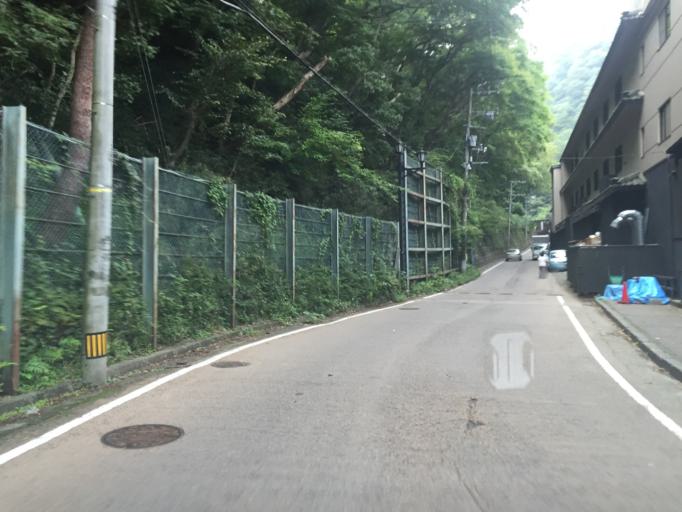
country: JP
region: Fukushima
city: Inawashiro
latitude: 37.4802
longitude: 139.9602
